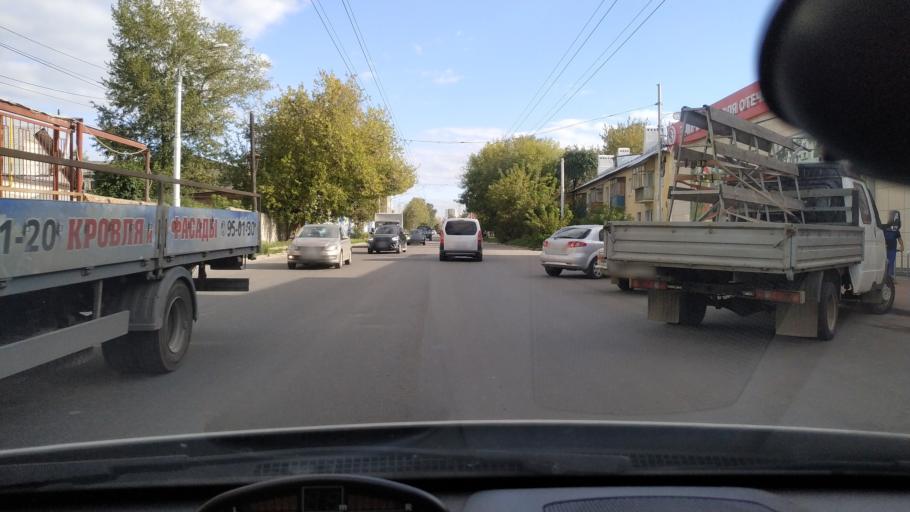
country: RU
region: Rjazan
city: Ryazan'
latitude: 54.6144
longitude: 39.6948
